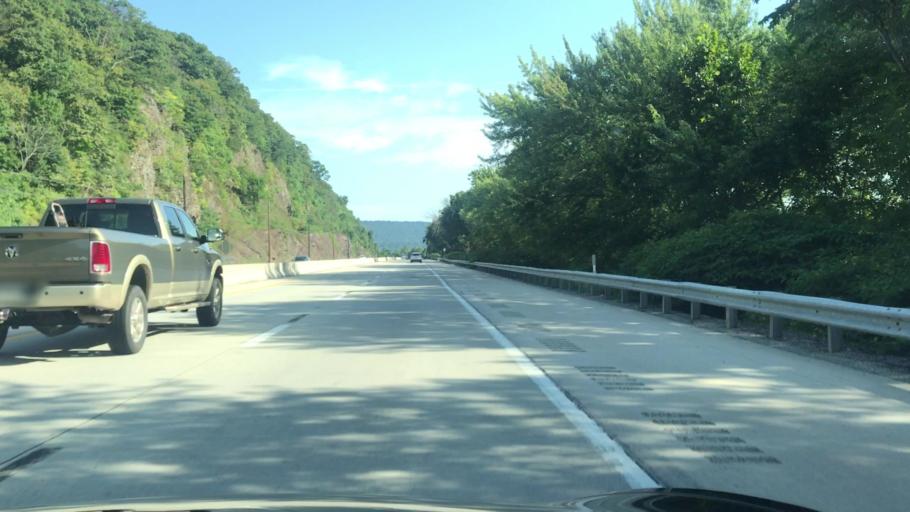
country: US
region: Pennsylvania
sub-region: Dauphin County
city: Matamoras
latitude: 40.4756
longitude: -76.9490
